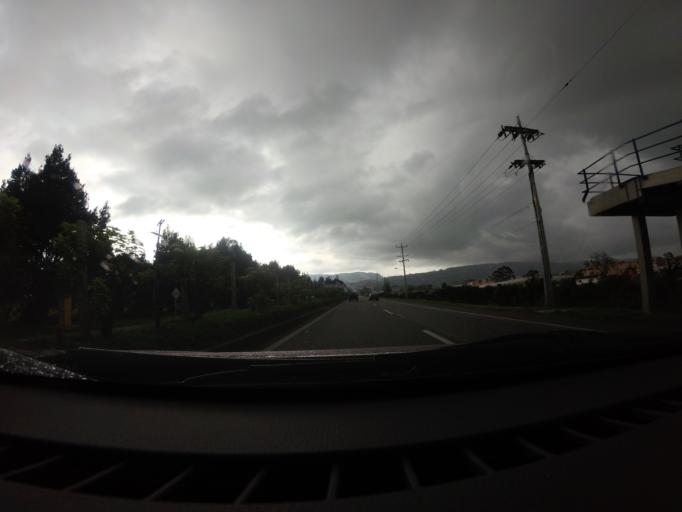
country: CO
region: Cundinamarca
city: El Rosal
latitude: 4.8404
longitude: -74.2589
